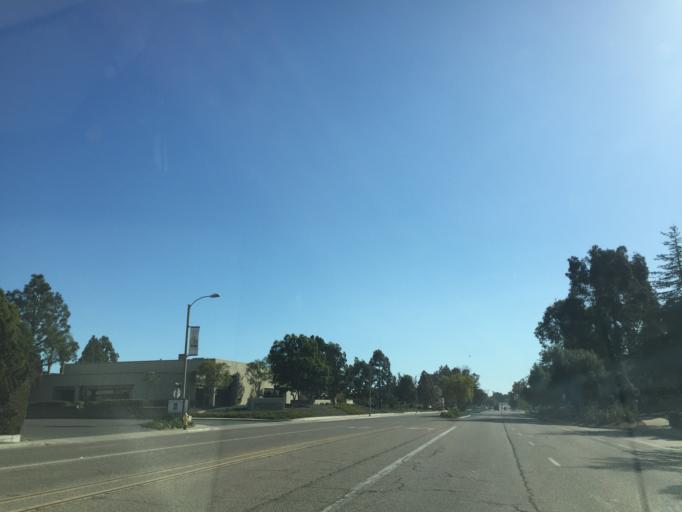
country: US
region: California
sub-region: Santa Barbara County
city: Isla Vista
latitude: 34.4285
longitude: -119.8698
